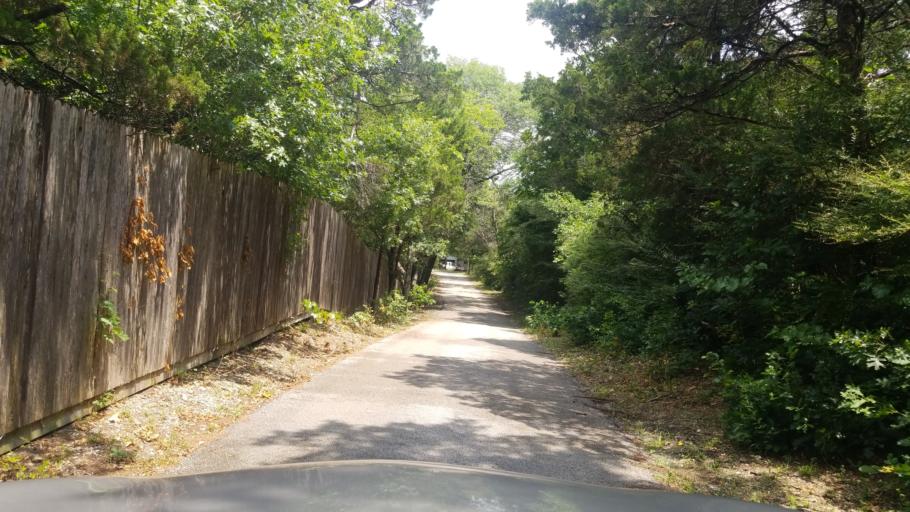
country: US
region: Texas
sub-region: Dallas County
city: Duncanville
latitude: 32.6825
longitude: -96.9245
